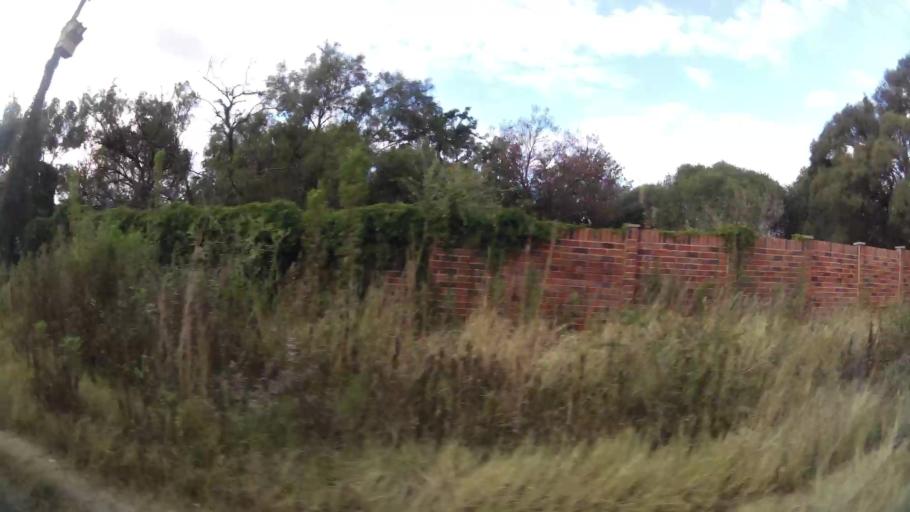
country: ZA
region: Orange Free State
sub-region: Mangaung Metropolitan Municipality
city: Bloemfontein
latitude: -29.0726
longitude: 26.2059
